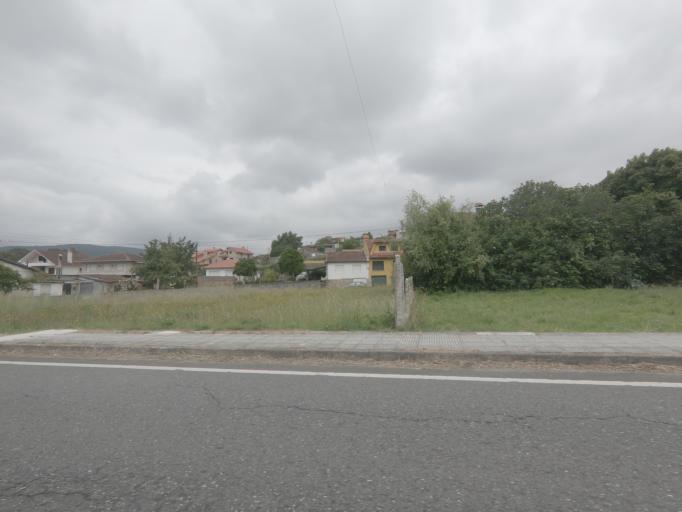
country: PT
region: Viana do Castelo
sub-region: Valenca
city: Valenca
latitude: 42.0386
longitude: -8.6536
